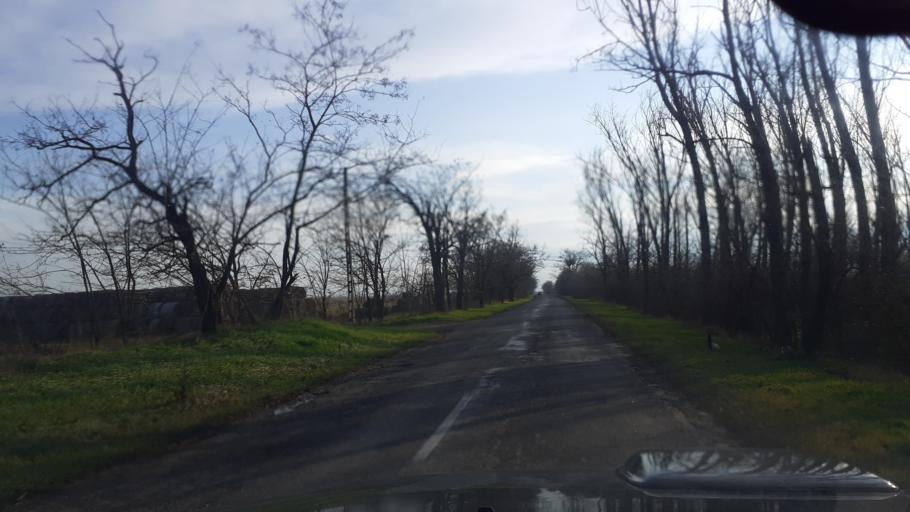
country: HU
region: Bacs-Kiskun
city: Kunszentmiklos
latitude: 47.0960
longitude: 19.0928
